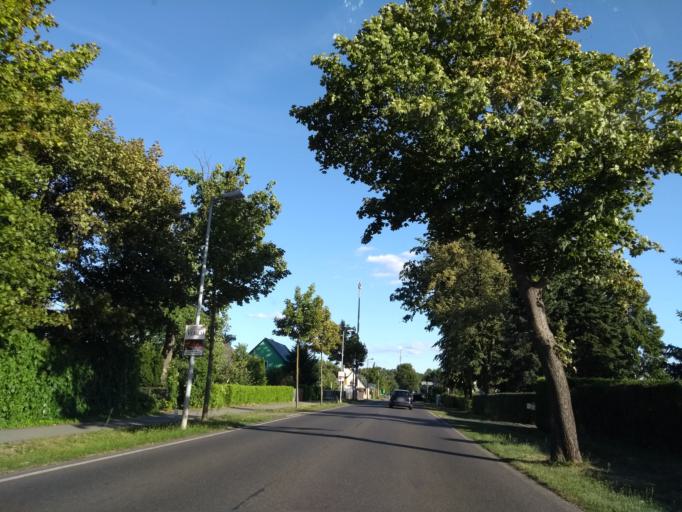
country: DE
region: Brandenburg
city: Lubbenau
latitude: 51.8698
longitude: 13.9169
